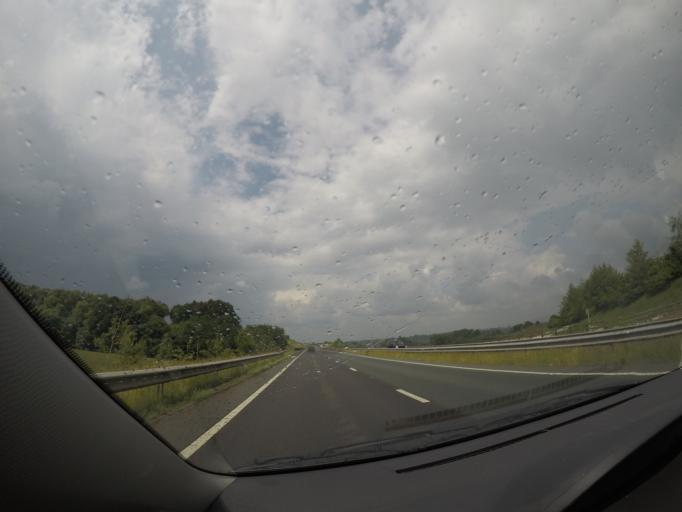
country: GB
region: England
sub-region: Cumbria
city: Appleby-in-Westmorland
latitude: 54.6391
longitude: -2.6141
